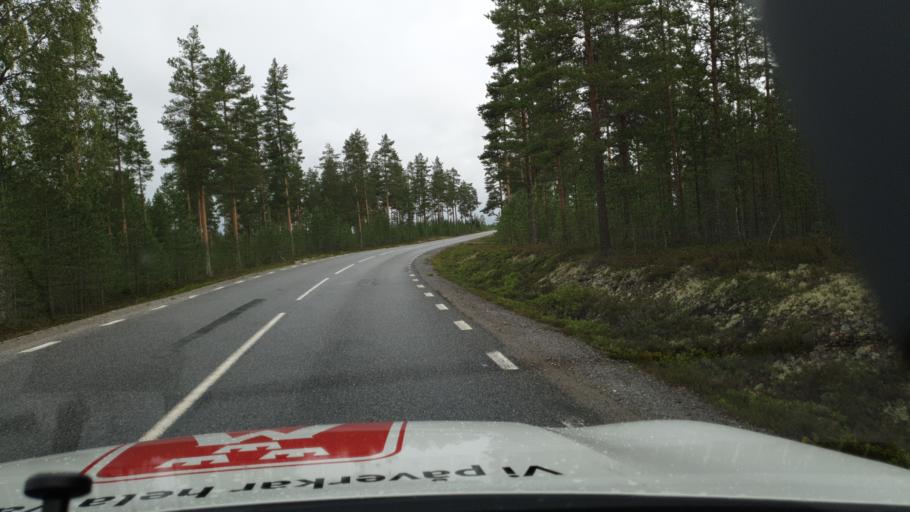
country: SE
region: Vaesterbotten
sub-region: Umea Kommun
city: Saevar
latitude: 63.9664
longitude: 20.5075
